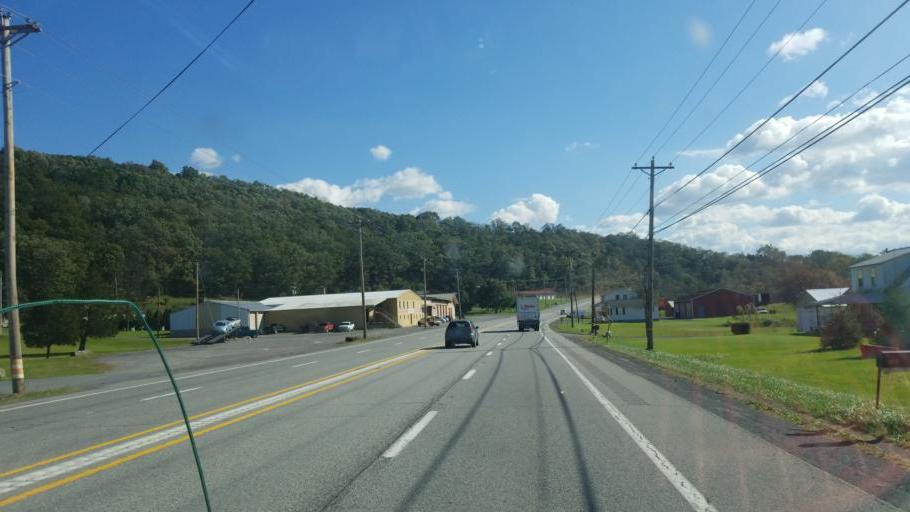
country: US
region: Pennsylvania
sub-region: Bedford County
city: Earlston
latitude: 40.0199
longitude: -78.3362
